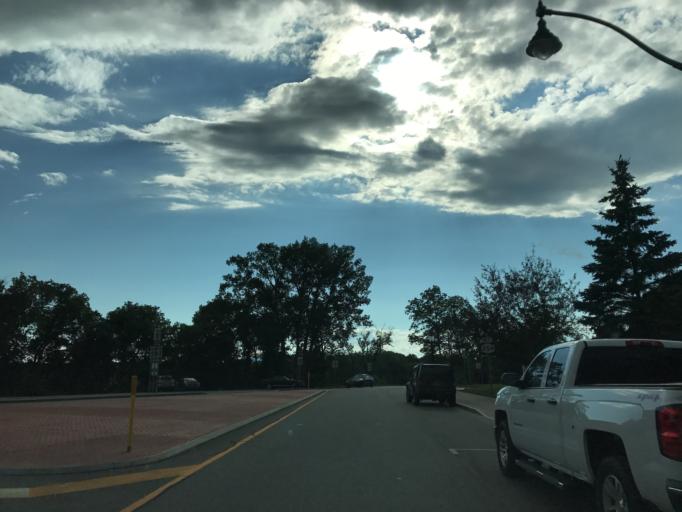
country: US
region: New York
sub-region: Washington County
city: Hudson Falls
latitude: 43.3020
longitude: -73.5869
